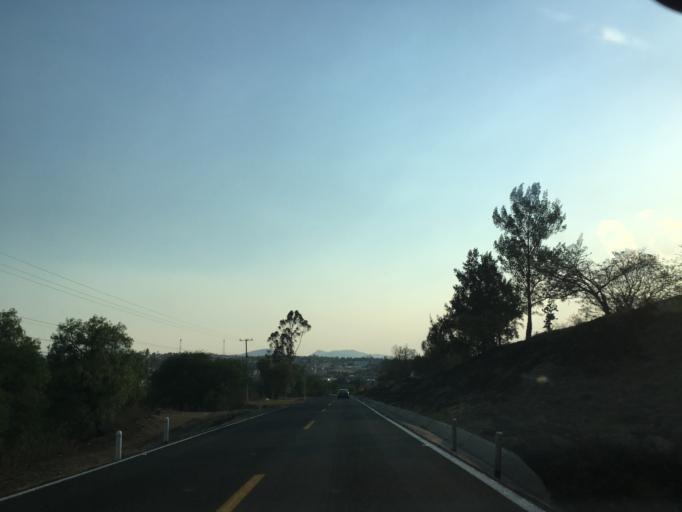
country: MX
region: Michoacan
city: Charo
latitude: 19.7565
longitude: -101.0381
